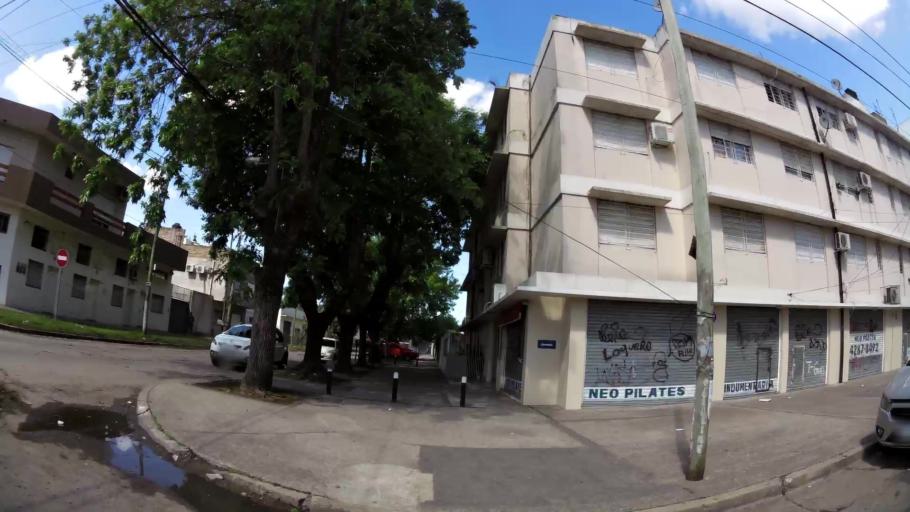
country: AR
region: Buenos Aires
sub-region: Partido de Quilmes
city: Quilmes
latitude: -34.8140
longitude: -58.2760
